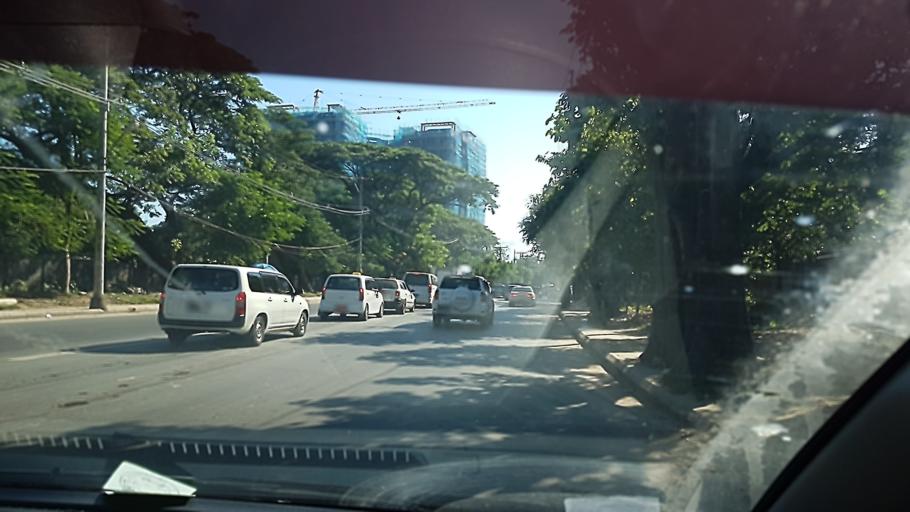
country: MM
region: Yangon
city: Yangon
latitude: 16.8577
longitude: 96.1276
